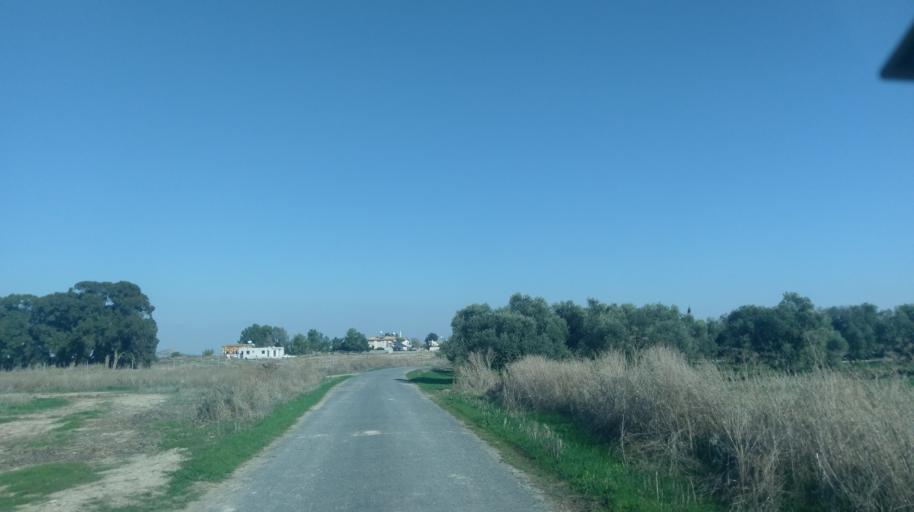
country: CY
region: Larnaka
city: Athienou
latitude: 35.0746
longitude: 33.5756
